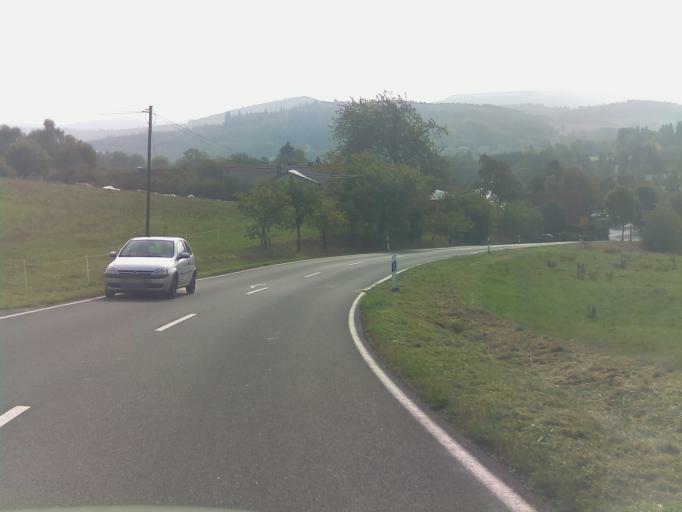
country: DE
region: Hesse
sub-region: Regierungsbezirk Kassel
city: Hilders
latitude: 50.5641
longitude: 9.9196
